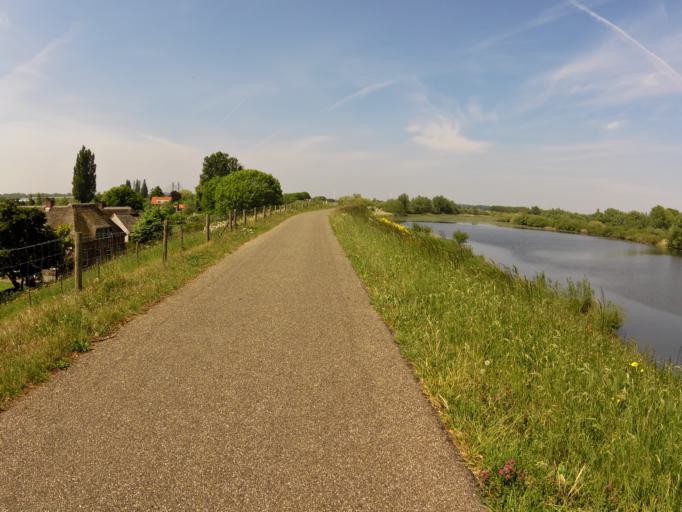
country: NL
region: Gelderland
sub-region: Gemeente Neerijnen
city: Neerijnen
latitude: 51.8059
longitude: 5.2848
